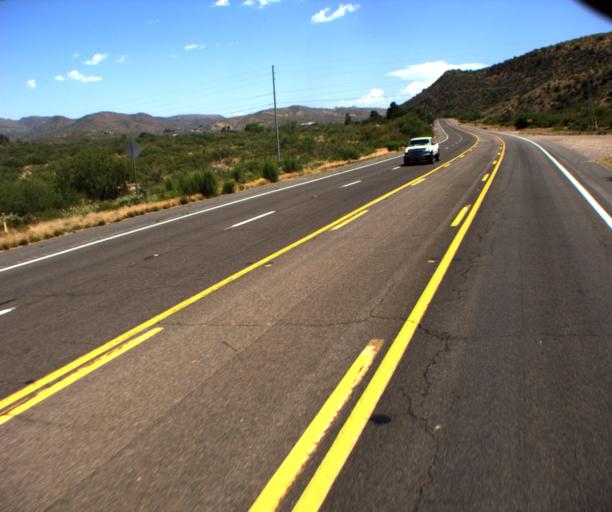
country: US
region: Arizona
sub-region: Gila County
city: Claypool
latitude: 33.4681
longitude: -110.8535
